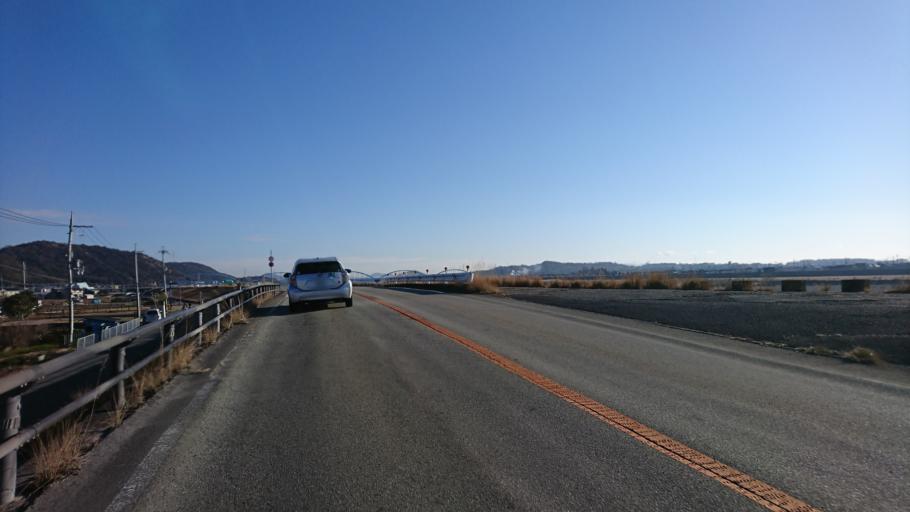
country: JP
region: Hyogo
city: Kakogawacho-honmachi
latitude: 34.7795
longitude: 134.8402
